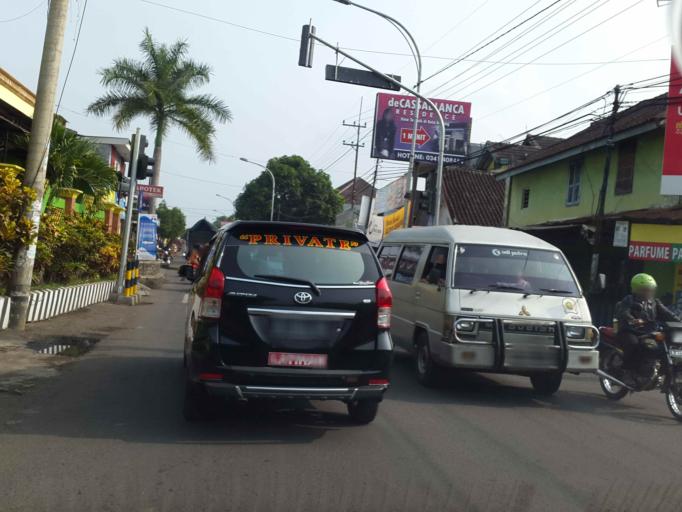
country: ID
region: East Java
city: Malang
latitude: -7.9745
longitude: 112.6724
